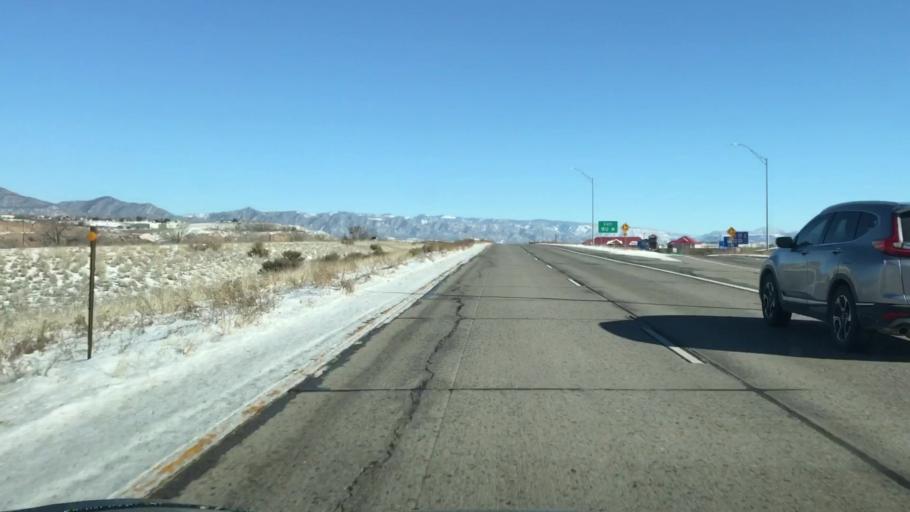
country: US
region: Colorado
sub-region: Garfield County
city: Rifle
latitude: 39.5225
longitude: -107.7829
